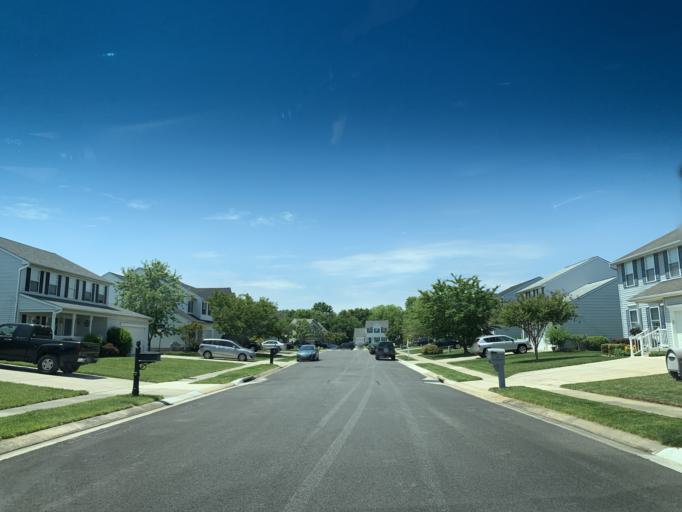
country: US
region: Maryland
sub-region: Harford County
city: Bel Air North
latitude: 39.5750
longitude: -76.3644
